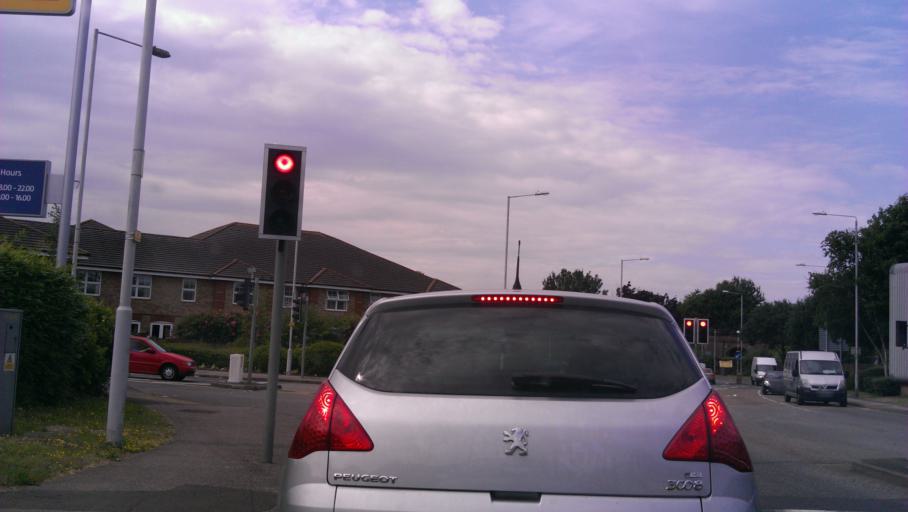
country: GB
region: England
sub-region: Kent
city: Sittingbourne
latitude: 51.3392
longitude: 0.7455
